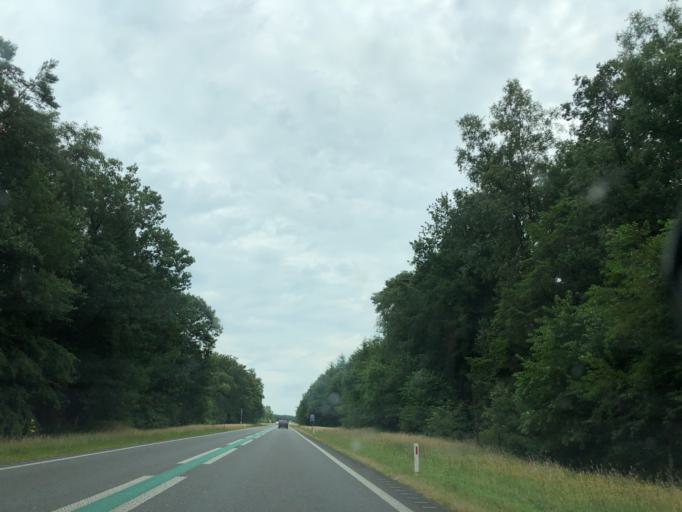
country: NL
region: Drenthe
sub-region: Gemeente Borger-Odoorn
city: Borger
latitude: 52.9572
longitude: 6.7816
